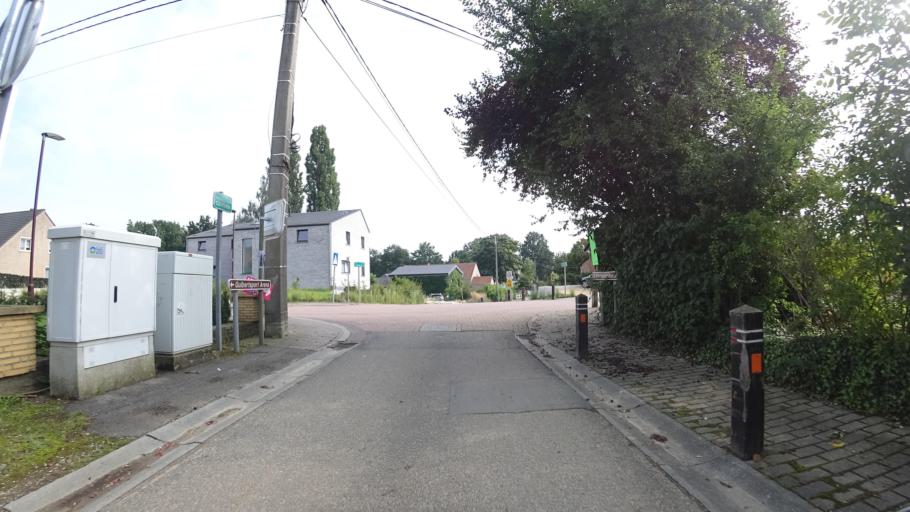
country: BE
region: Wallonia
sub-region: Province du Brabant Wallon
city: Mont-Saint-Guibert
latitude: 50.6405
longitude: 4.6189
